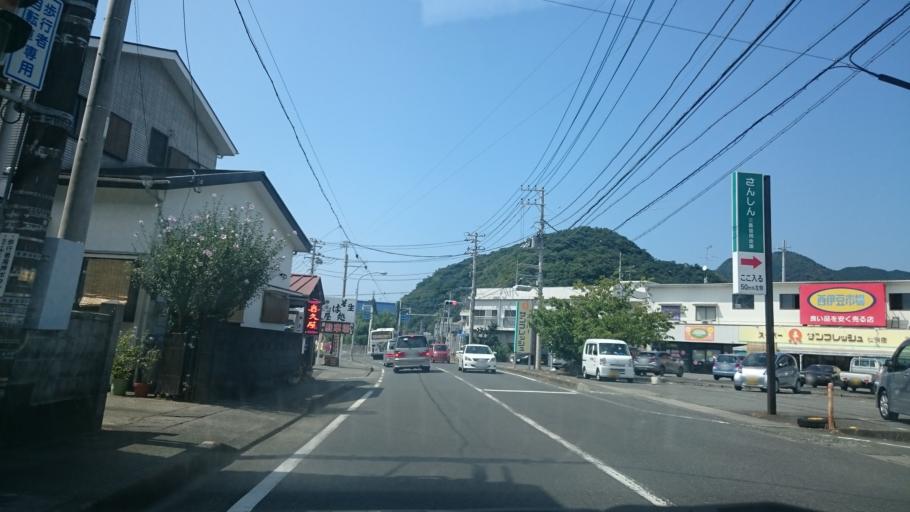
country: JP
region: Shizuoka
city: Heda
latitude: 34.7697
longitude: 138.7762
